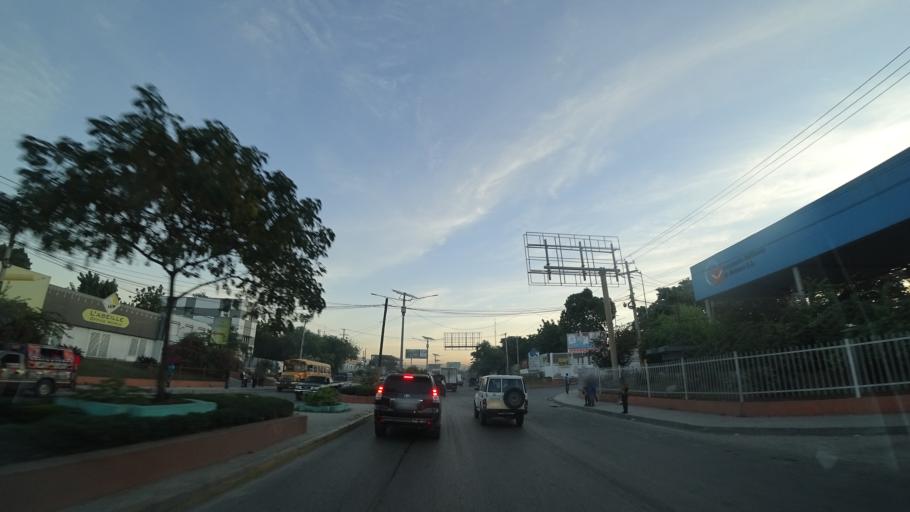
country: HT
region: Ouest
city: Delmas 73
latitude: 18.5695
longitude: -72.3096
